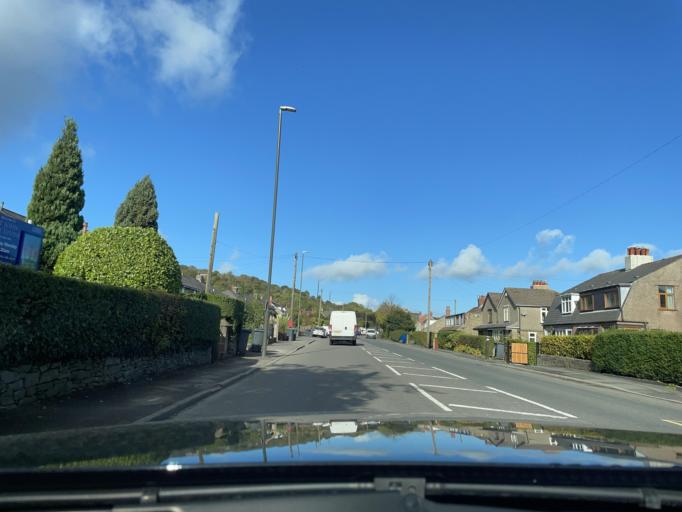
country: GB
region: England
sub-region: Derbyshire
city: New Mills
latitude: 53.3530
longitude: -1.9965
